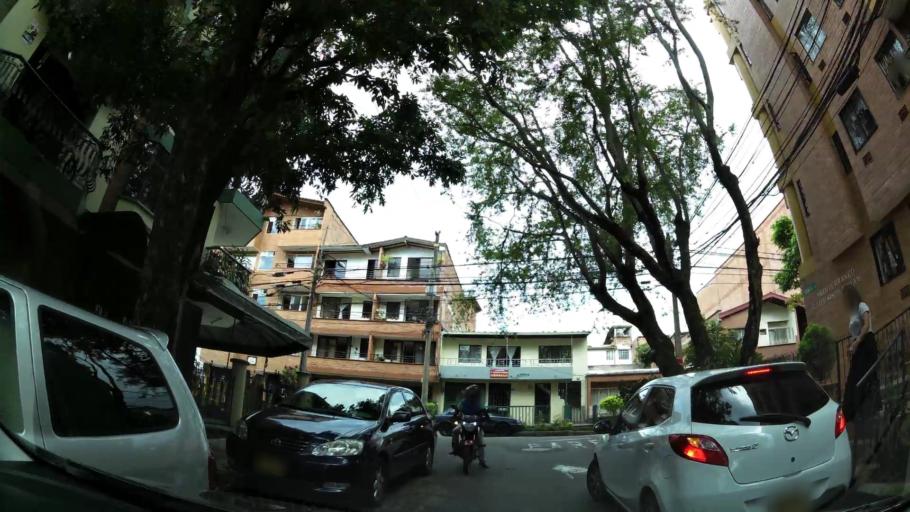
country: CO
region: Antioquia
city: Envigado
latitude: 6.1638
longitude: -75.5906
